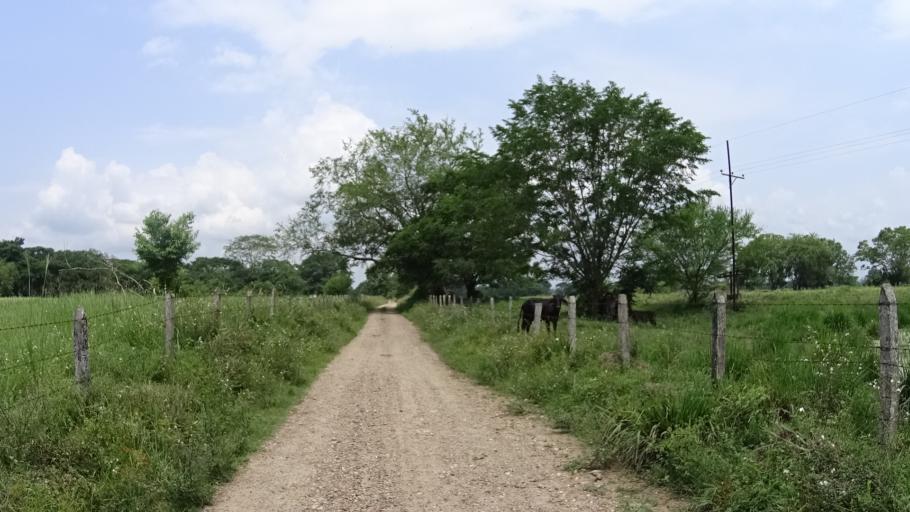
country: CO
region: Cundinamarca
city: Puerto Salgar
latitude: 5.5423
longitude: -74.6669
